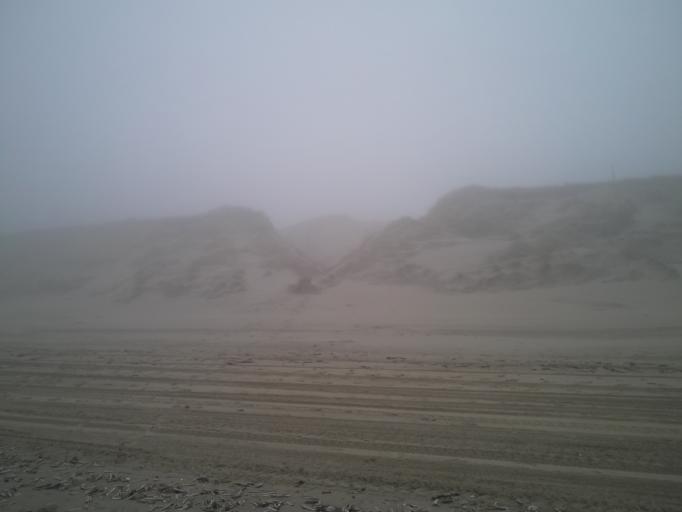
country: NL
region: North Holland
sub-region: Gemeente Zandvoort
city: Zandvoort
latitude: 52.3353
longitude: 4.4991
